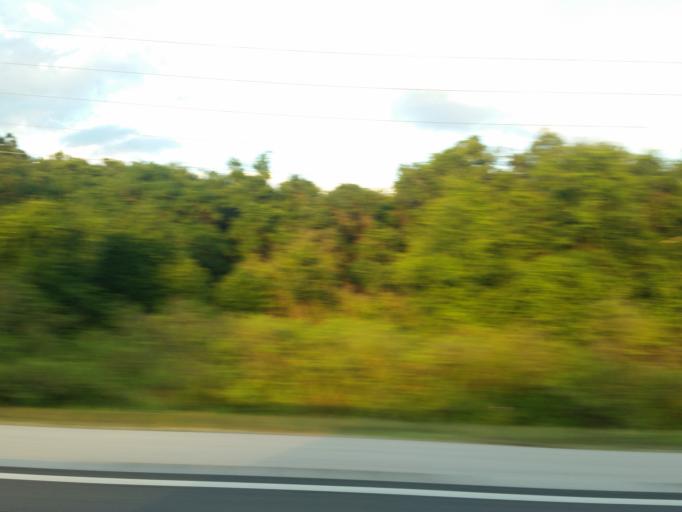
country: US
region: Florida
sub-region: Sarasota County
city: Lake Sarasota
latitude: 27.2821
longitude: -82.4486
